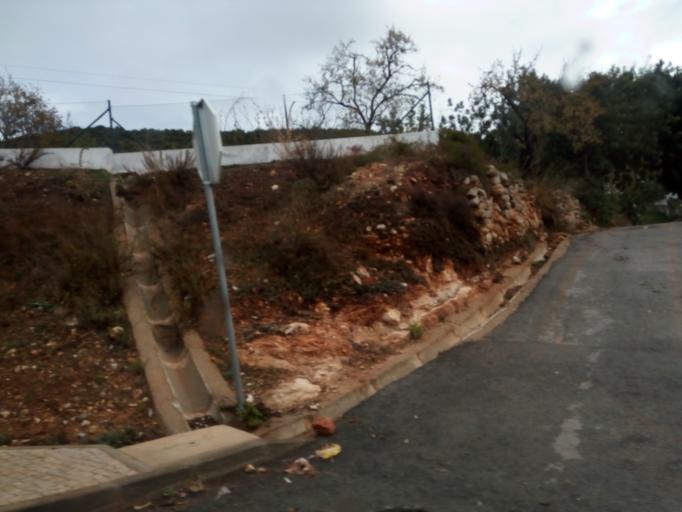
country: PT
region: Faro
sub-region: Loule
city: Loule
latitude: 37.1095
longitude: -8.0046
